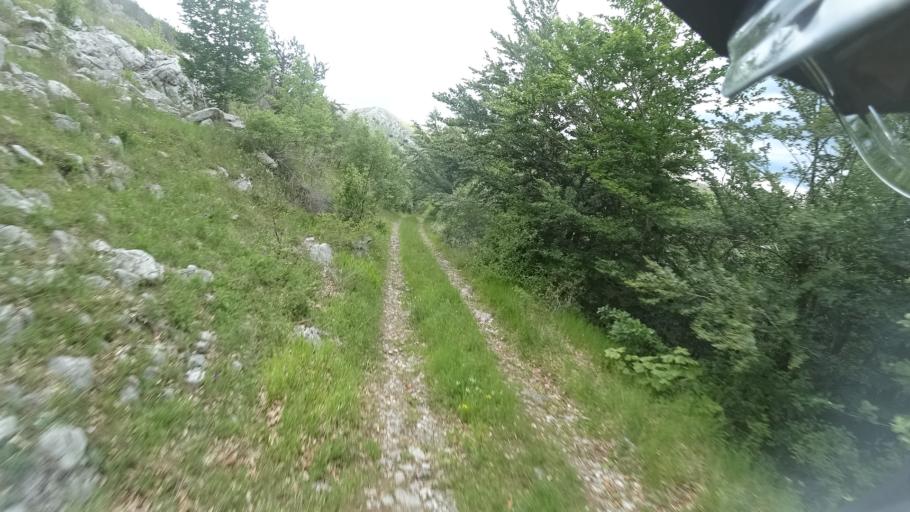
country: HR
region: Zadarska
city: Obrovac
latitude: 44.2622
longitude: 15.7246
